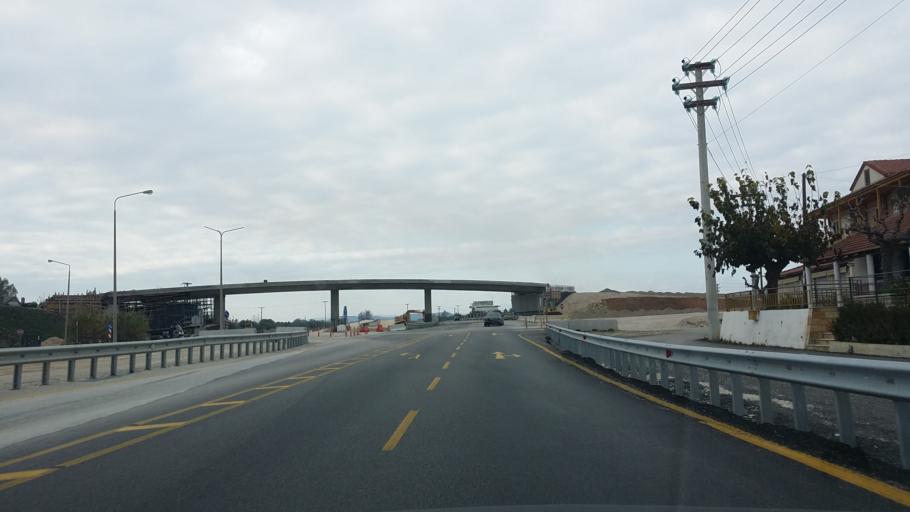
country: GR
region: West Greece
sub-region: Nomos Aitolias kai Akarnanias
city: Mesolongi
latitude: 38.3974
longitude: 21.4164
